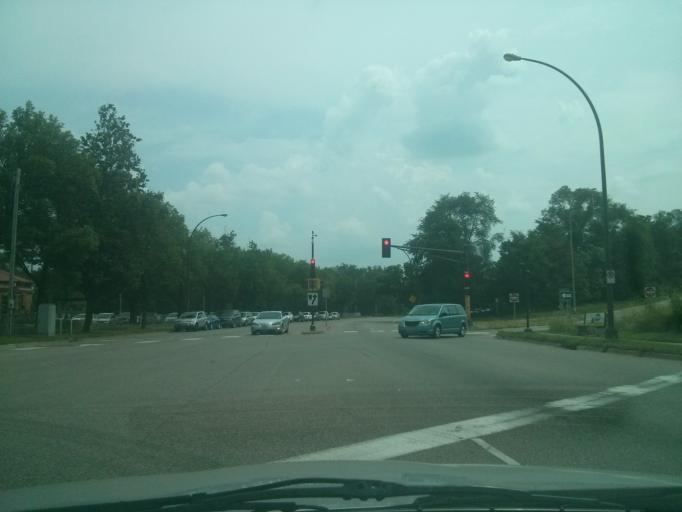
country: US
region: Minnesota
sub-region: Ramsey County
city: Saint Paul
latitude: 44.9272
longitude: -93.0692
